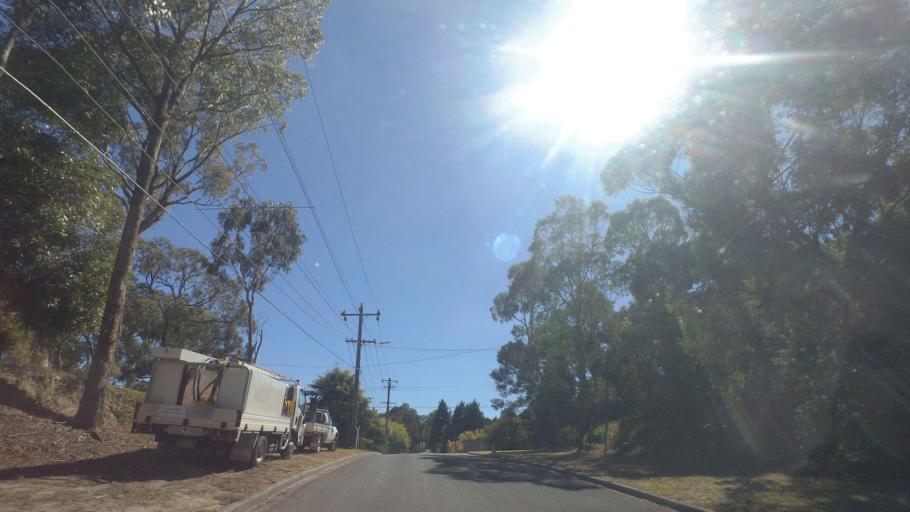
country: AU
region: Victoria
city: Mitcham
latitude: -37.8051
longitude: 145.2087
